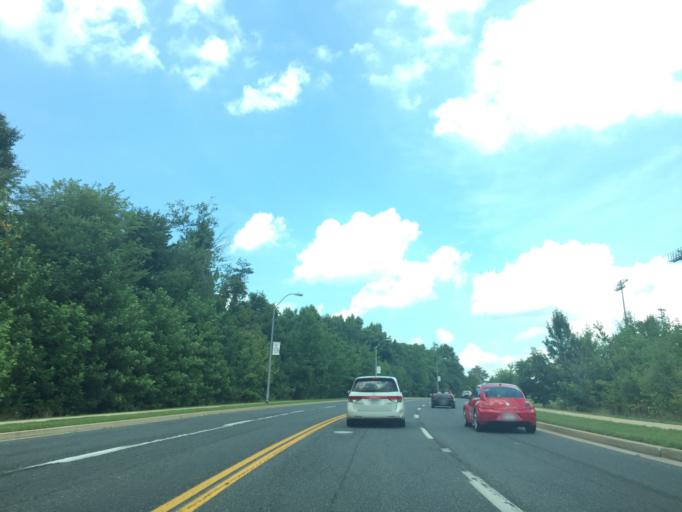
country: US
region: Maryland
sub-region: Baltimore County
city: Perry Hall
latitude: 39.3942
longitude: -76.4539
